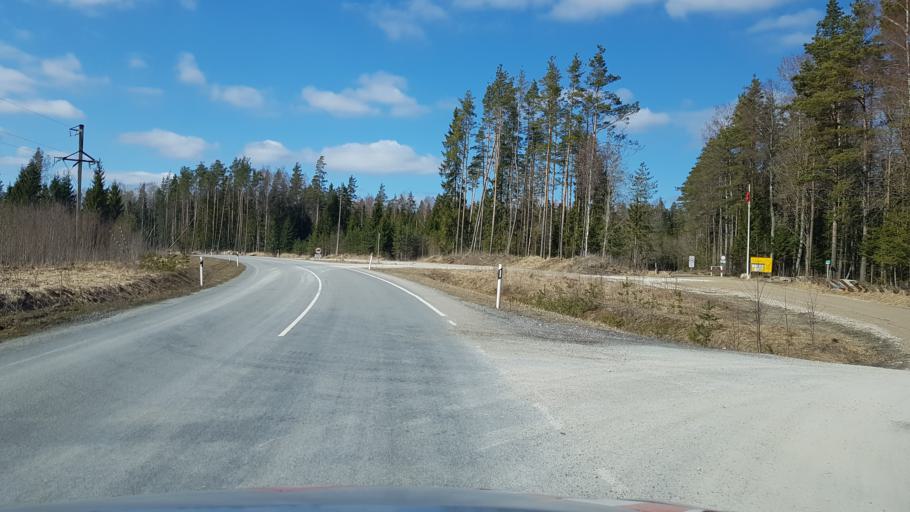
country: EE
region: Laeaene-Virumaa
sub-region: Tapa vald
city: Tapa
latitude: 59.2773
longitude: 25.9123
